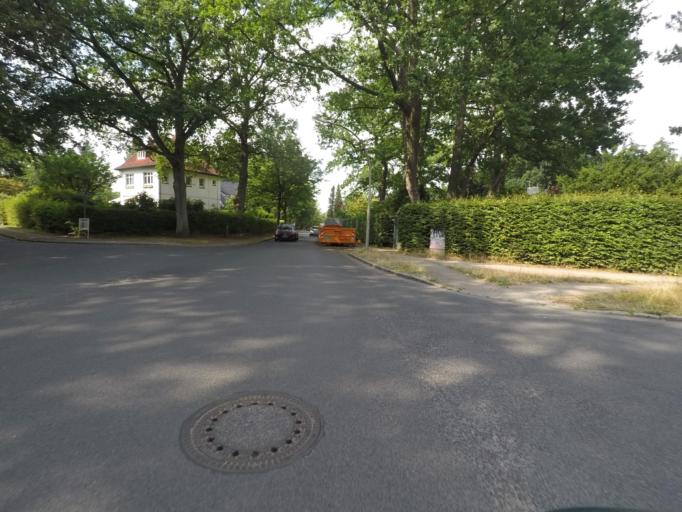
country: DE
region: Hamburg
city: Wellingsbuettel
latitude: 53.6358
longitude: 10.0653
